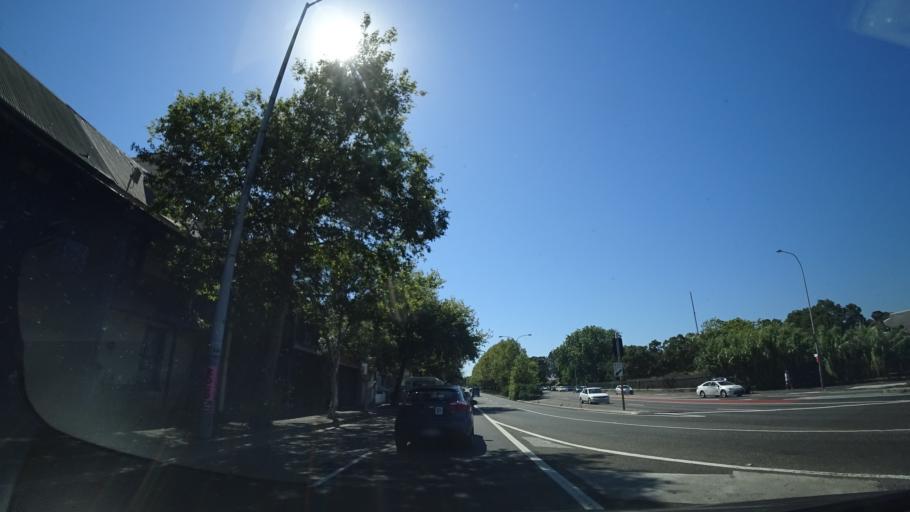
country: AU
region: New South Wales
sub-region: Woollahra
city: Woollahra
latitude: -33.8895
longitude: 151.2333
